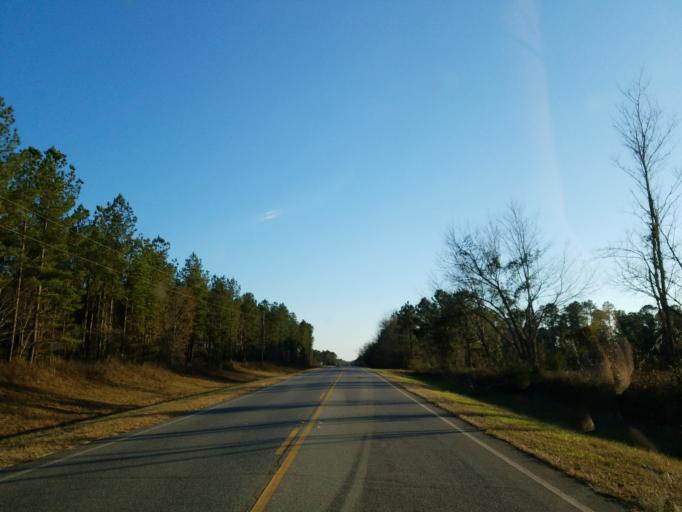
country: US
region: Georgia
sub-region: Turner County
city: Ashburn
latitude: 31.6887
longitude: -83.8080
